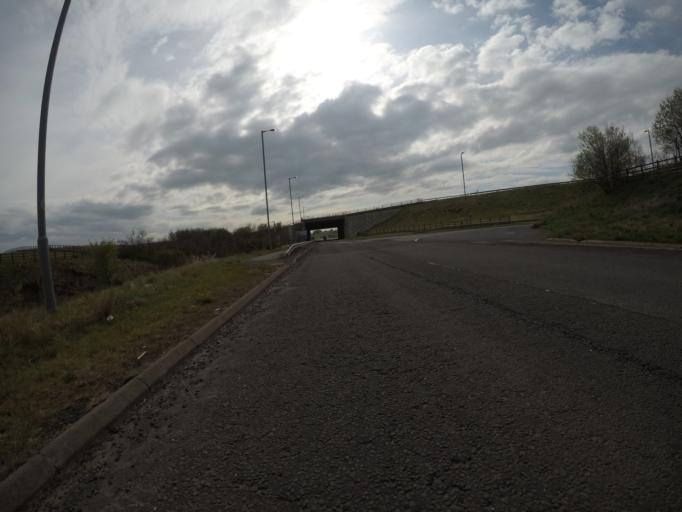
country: GB
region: Scotland
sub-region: East Ayrshire
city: Galston
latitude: 55.6929
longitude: -4.3986
